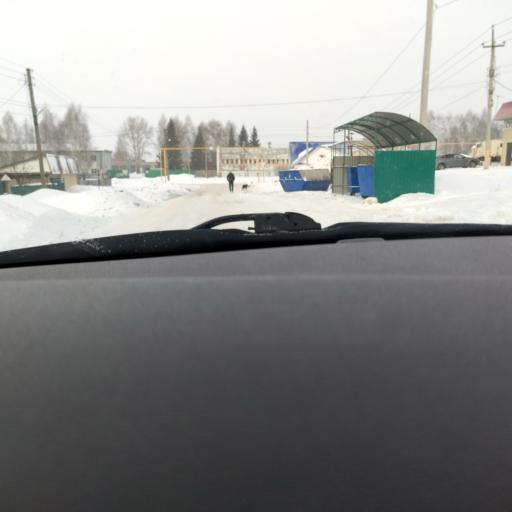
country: RU
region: Bashkortostan
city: Blagoveshchensk
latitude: 55.0280
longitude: 56.0029
